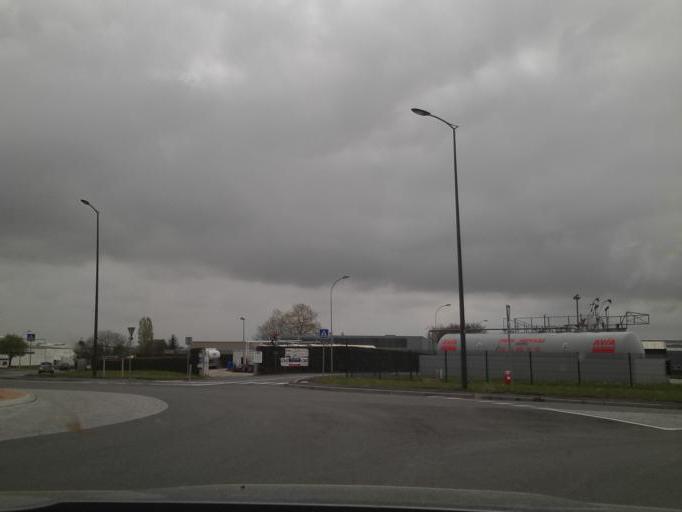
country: FR
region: Pays de la Loire
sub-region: Departement de la Vendee
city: Fontenay-le-Comte
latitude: 46.4522
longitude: -0.8017
